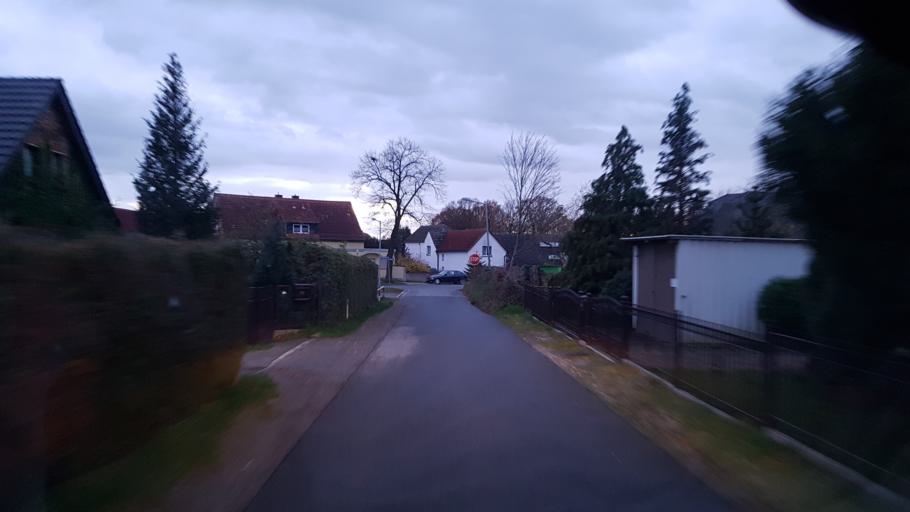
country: DE
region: Brandenburg
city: Lauchhammer
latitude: 51.5138
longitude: 13.7029
